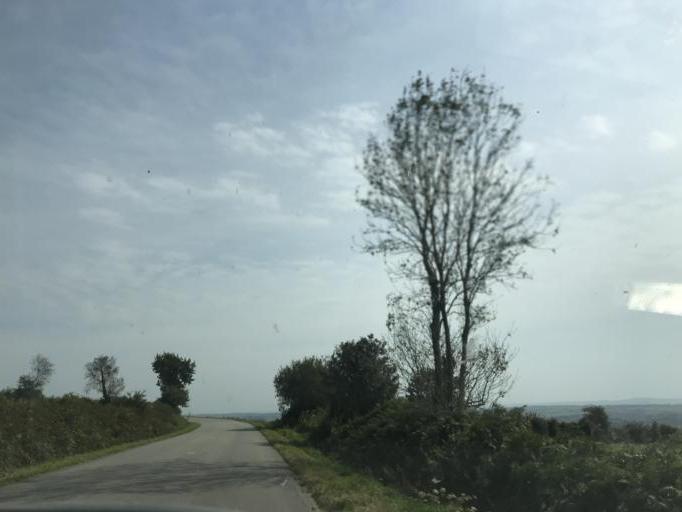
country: FR
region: Brittany
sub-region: Departement du Finistere
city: Loperec
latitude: 48.2945
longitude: -4.0620
